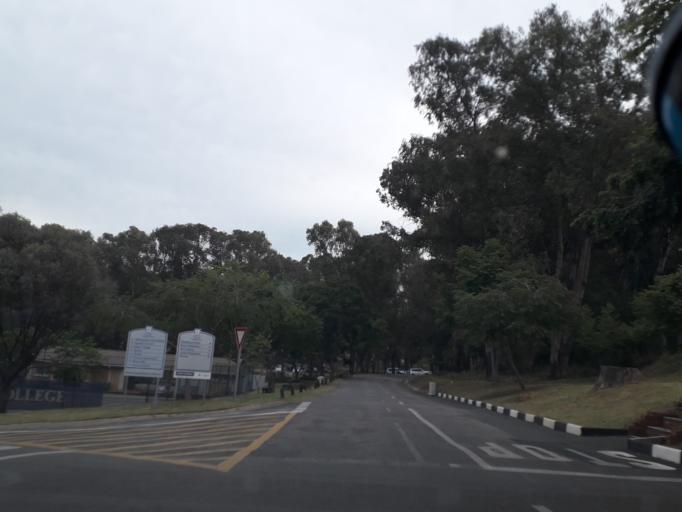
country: ZA
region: Gauteng
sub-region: City of Johannesburg Metropolitan Municipality
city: Johannesburg
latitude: -26.0870
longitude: 28.0120
